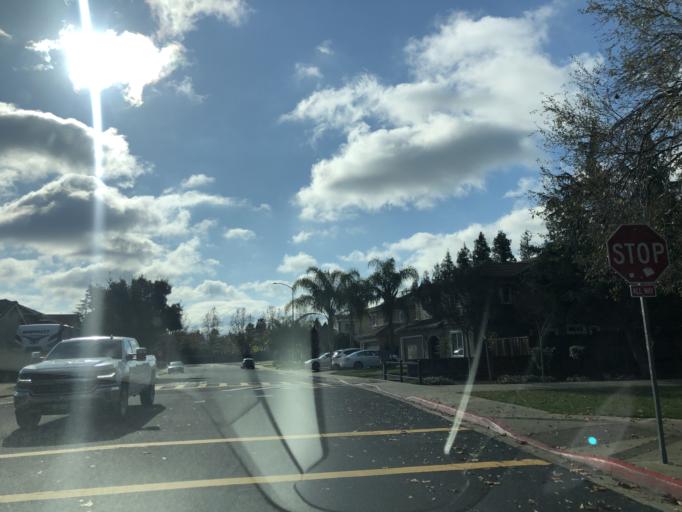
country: US
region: California
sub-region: Contra Costa County
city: Brentwood
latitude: 37.9410
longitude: -121.7336
